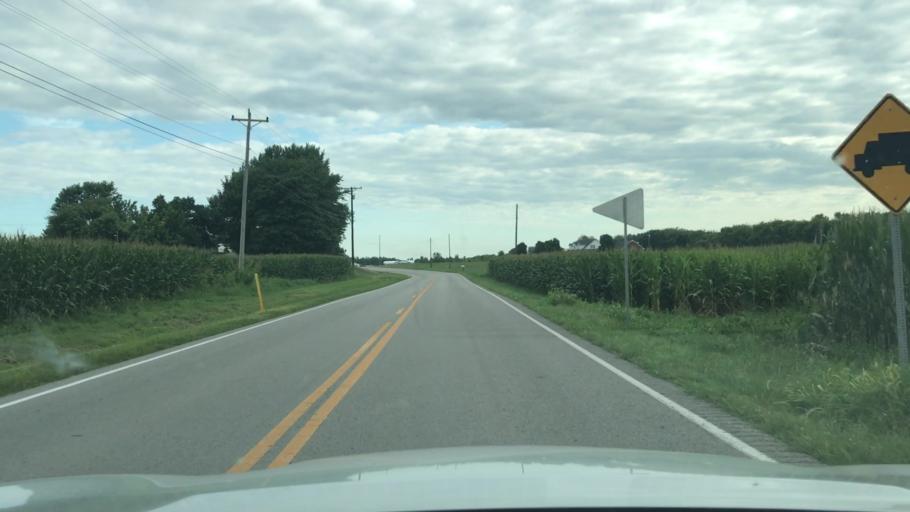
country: US
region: Kentucky
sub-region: Todd County
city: Elkton
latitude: 36.7802
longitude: -87.1638
